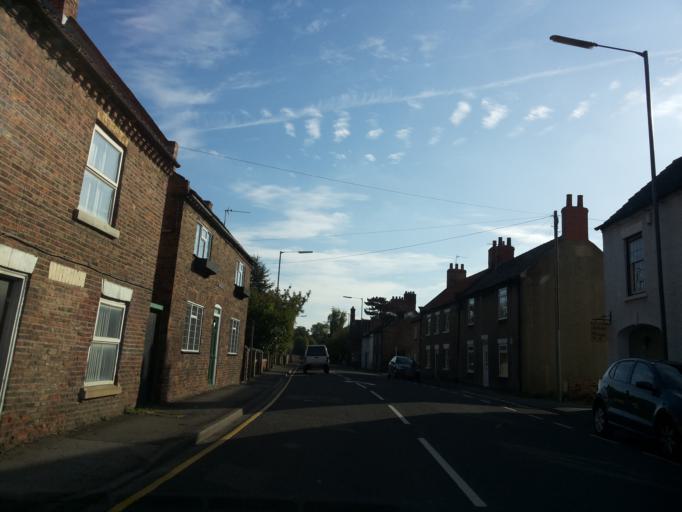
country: GB
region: England
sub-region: East Riding of Yorkshire
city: Snaith
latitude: 53.7076
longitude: -1.0207
